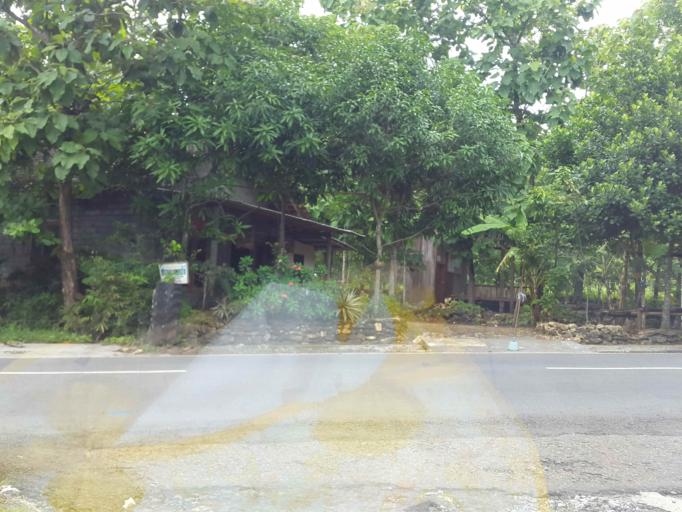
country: ID
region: Daerah Istimewa Yogyakarta
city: Wonosari
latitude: -7.9613
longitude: 110.5887
